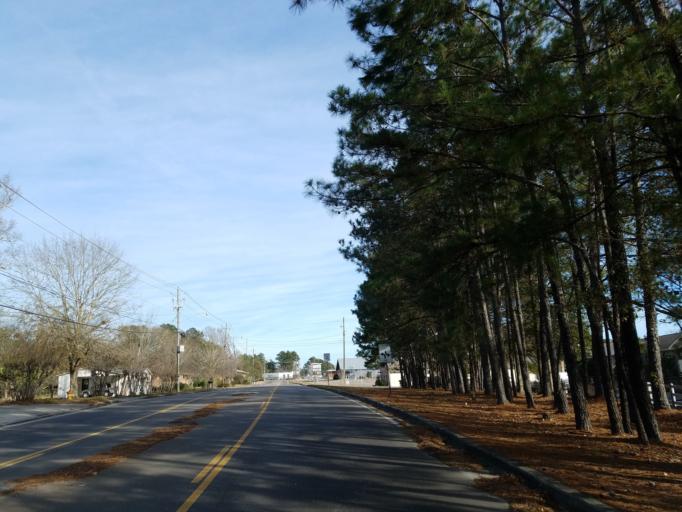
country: US
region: Mississippi
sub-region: Lamar County
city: Arnold Line
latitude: 31.3359
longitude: -89.3501
